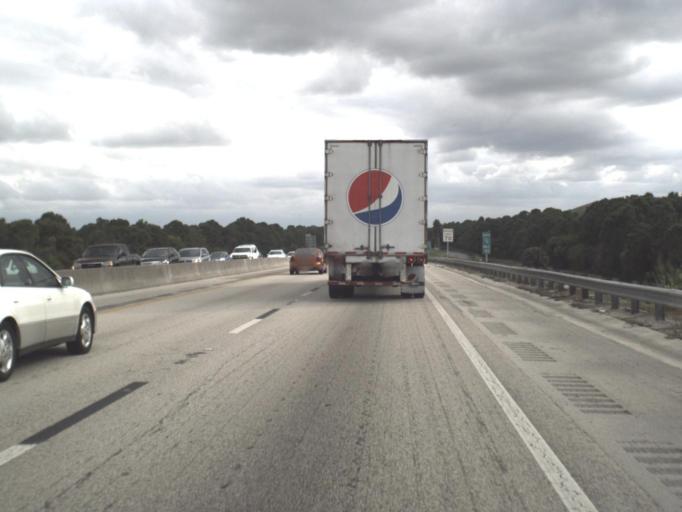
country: US
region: Florida
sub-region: Palm Beach County
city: Palm Beach Gardens
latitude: 26.7941
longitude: -80.1319
